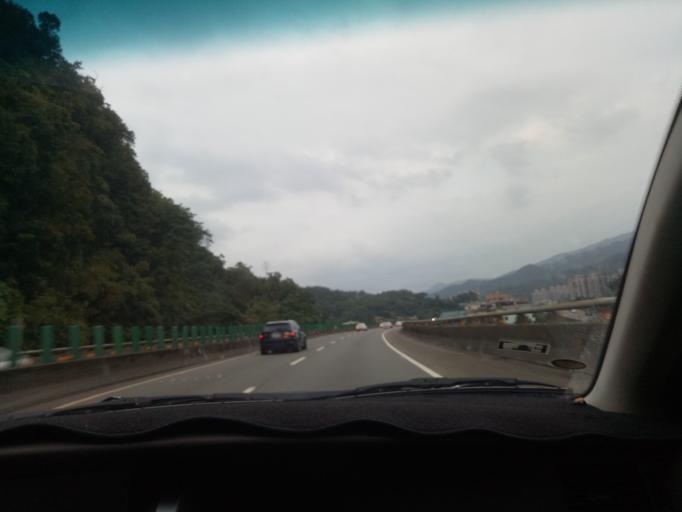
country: TW
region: Taiwan
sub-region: Keelung
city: Keelung
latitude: 25.1031
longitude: 121.7426
